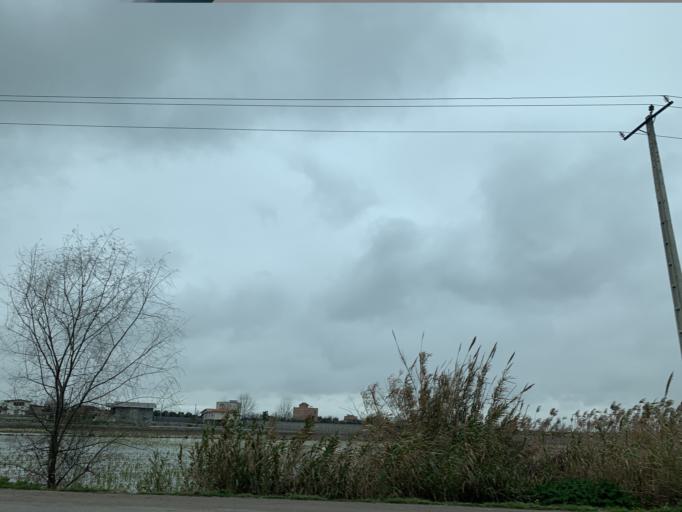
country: IR
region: Mazandaran
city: Babol
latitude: 36.5227
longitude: 52.6041
